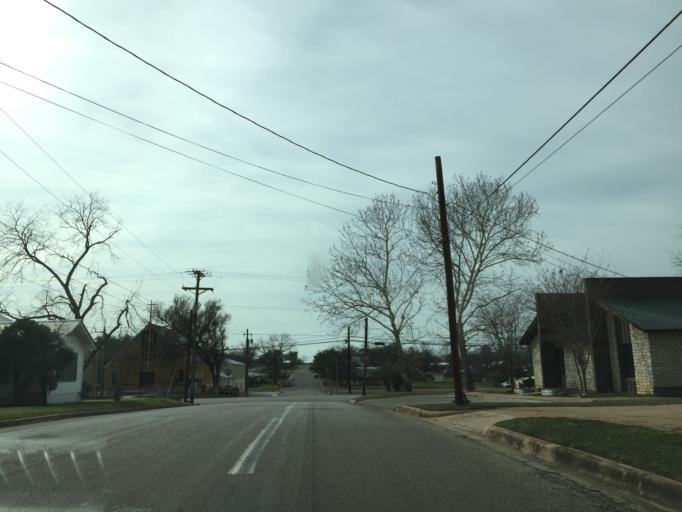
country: US
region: Texas
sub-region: Llano County
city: Llano
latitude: 30.7444
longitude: -98.6753
